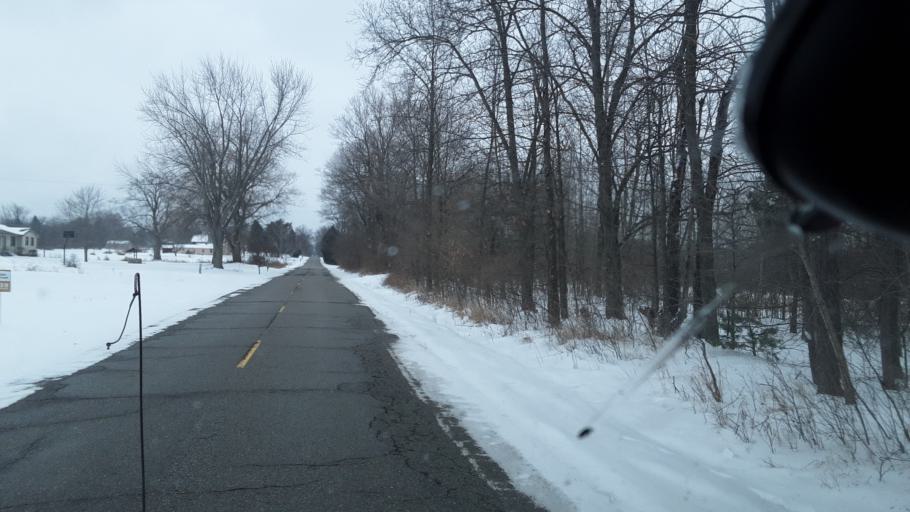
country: US
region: Michigan
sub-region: Ingham County
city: Leslie
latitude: 42.4545
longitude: -84.3941
